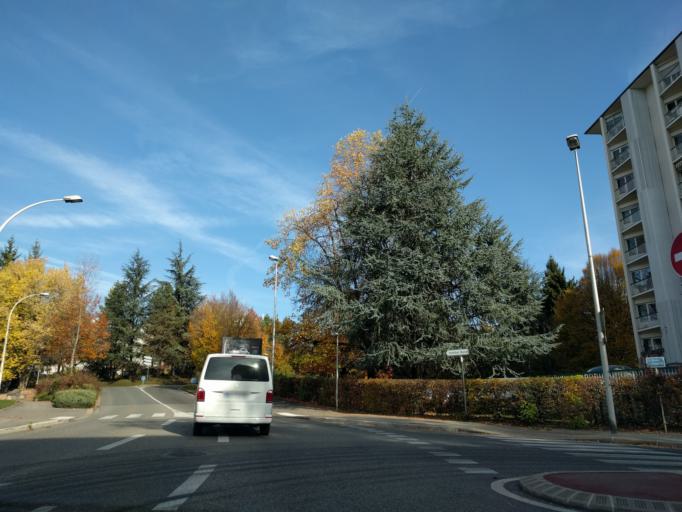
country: FR
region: Rhone-Alpes
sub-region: Departement de la Haute-Savoie
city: Annecy-le-Vieux
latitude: 45.9207
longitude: 6.1330
